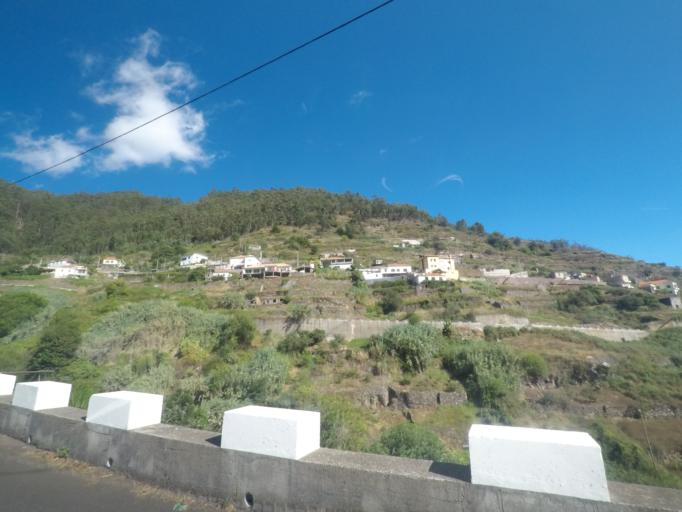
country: PT
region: Madeira
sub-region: Ribeira Brava
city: Campanario
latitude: 32.6784
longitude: -17.0219
